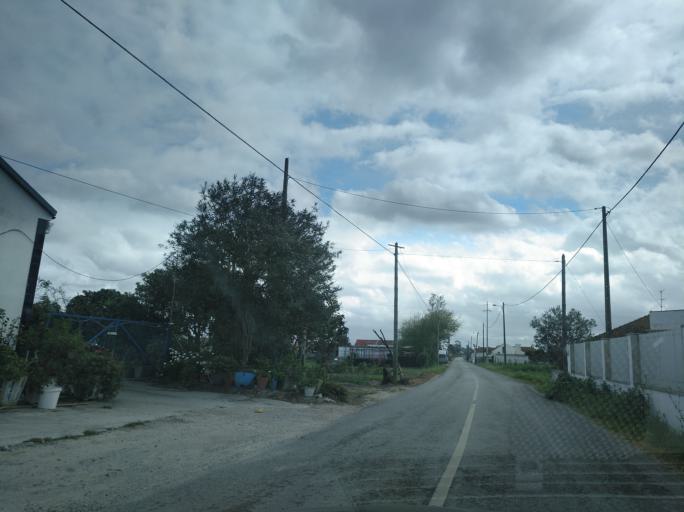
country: PT
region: Setubal
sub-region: Palmela
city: Pinhal Novo
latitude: 38.6753
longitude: -8.9196
